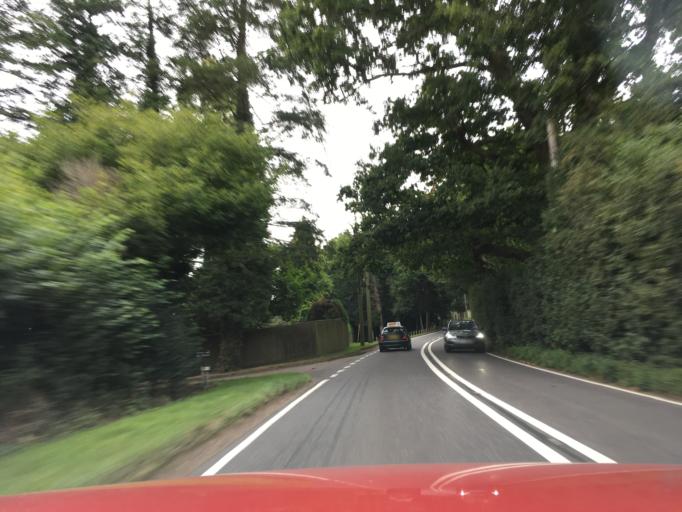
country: GB
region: England
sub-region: Hampshire
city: Petersfield
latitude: 51.0121
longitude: -0.9072
